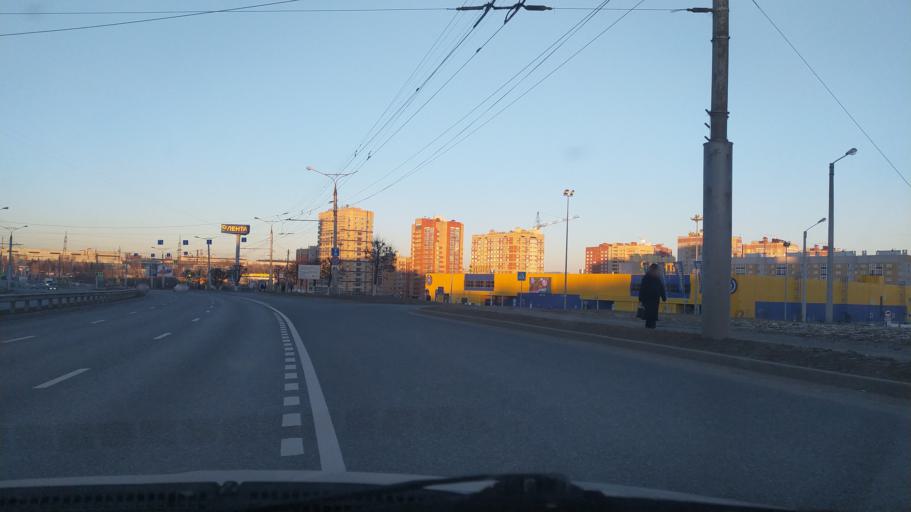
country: RU
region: Chuvashia
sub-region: Cheboksarskiy Rayon
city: Cheboksary
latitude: 56.1079
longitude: 47.3271
